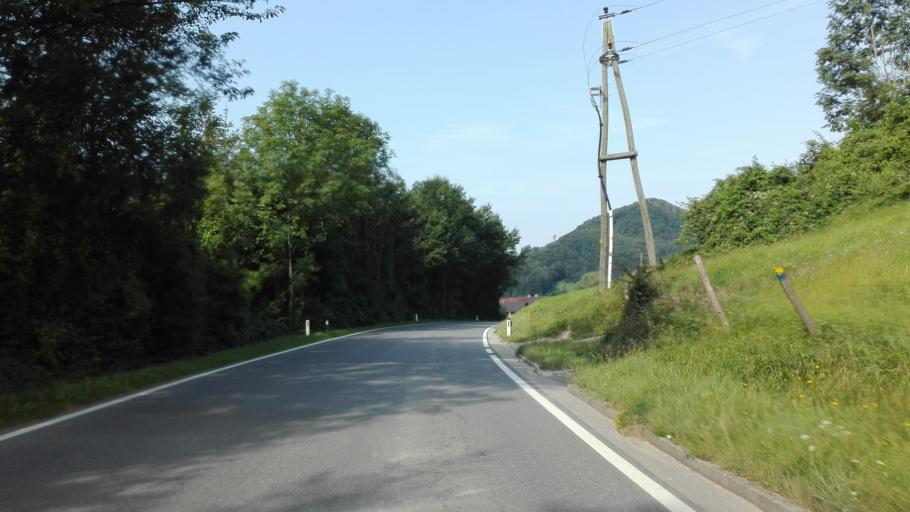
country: AT
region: Lower Austria
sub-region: Politischer Bezirk Sankt Polten
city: Rabenstein an der Pielach
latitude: 48.0316
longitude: 15.4771
